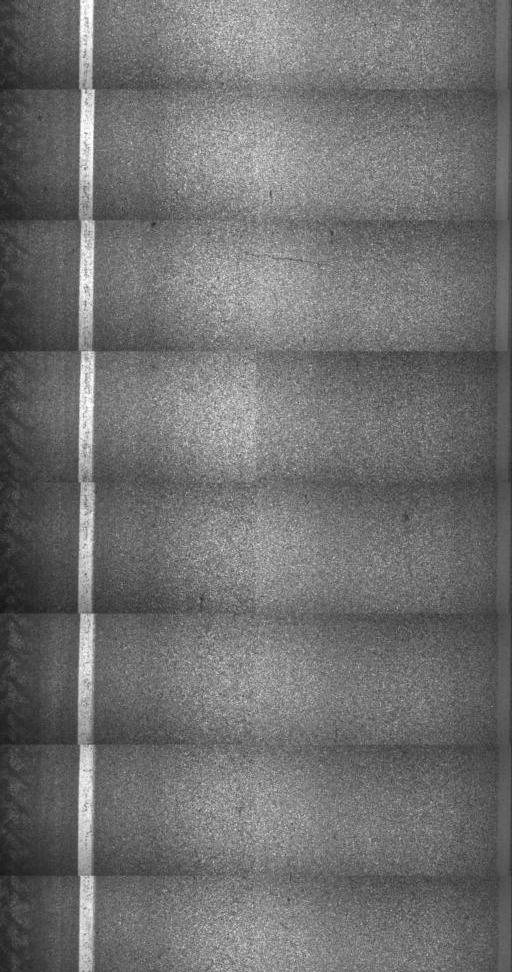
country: US
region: Vermont
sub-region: Lamoille County
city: Johnson
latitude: 44.7640
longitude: -72.5965
